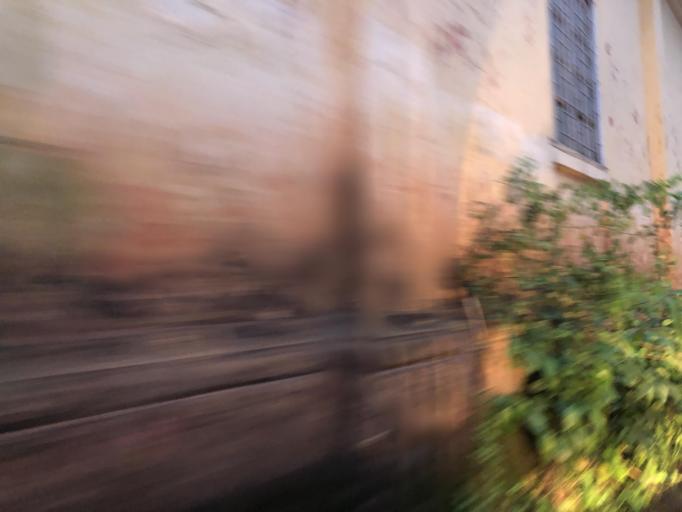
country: IN
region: Goa
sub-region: North Goa
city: Serula
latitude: 15.5514
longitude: 73.8232
